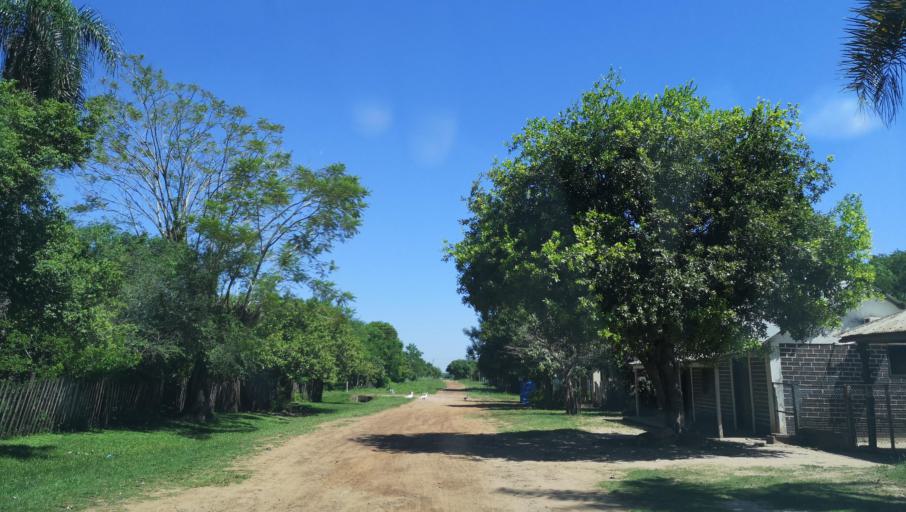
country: PY
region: Caaguazu
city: Carayao
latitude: -25.1928
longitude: -56.3997
